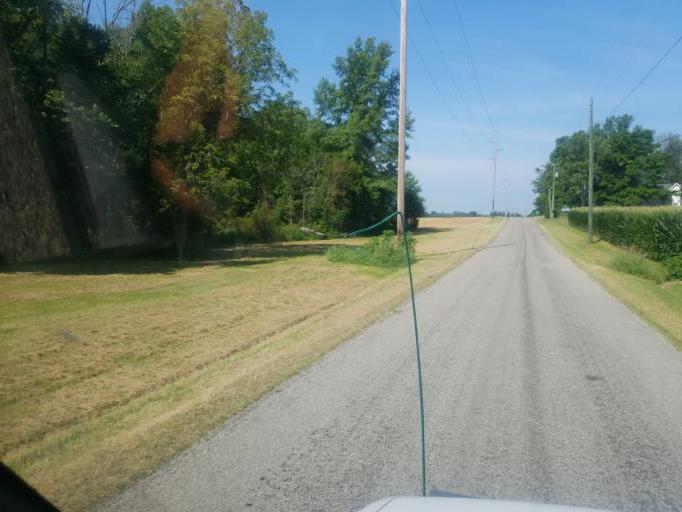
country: US
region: Ohio
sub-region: Union County
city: Marysville
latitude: 40.2876
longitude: -83.3706
